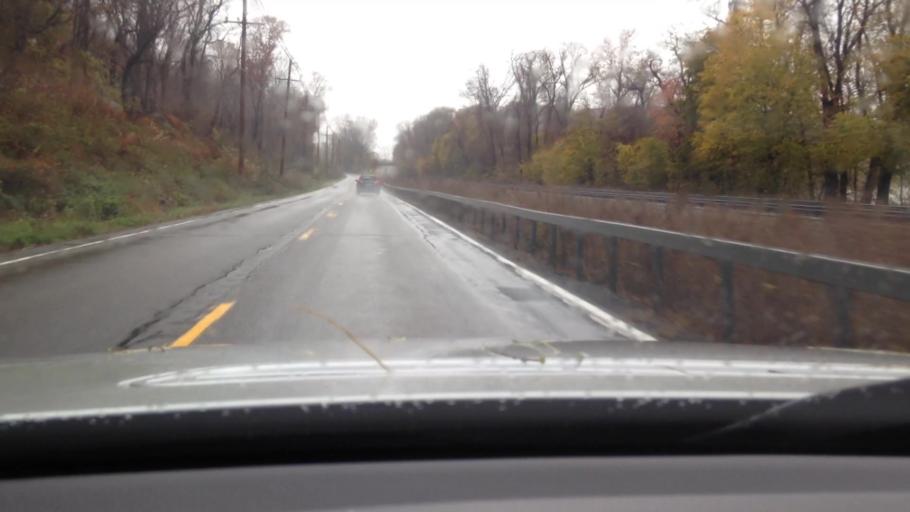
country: US
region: New York
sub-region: Putnam County
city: Cold Spring
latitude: 41.4310
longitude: -73.9689
